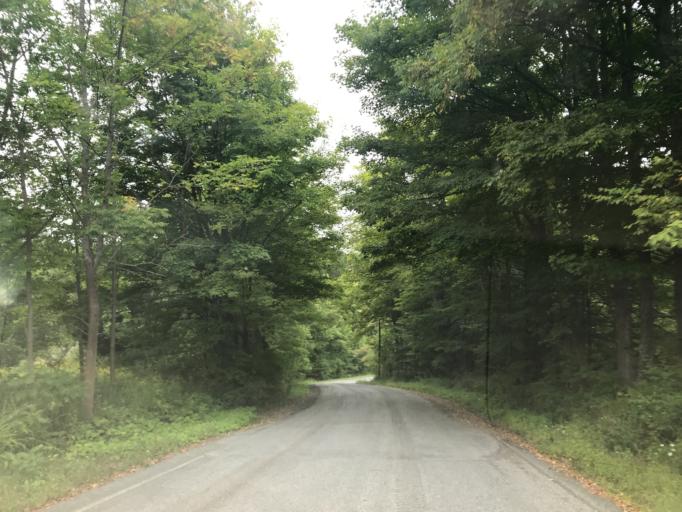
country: US
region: New York
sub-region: Delaware County
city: Stamford
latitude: 42.5127
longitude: -74.6272
